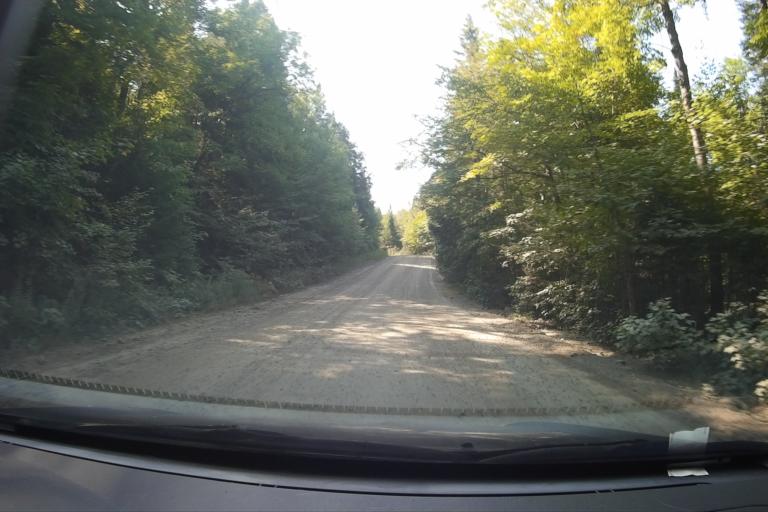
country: CA
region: Ontario
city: Huntsville
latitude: 45.5486
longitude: -78.6955
